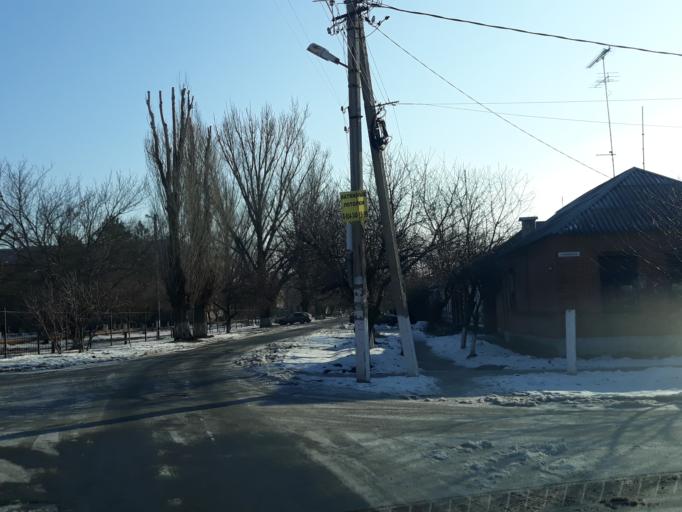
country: RU
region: Rostov
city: Taganrog
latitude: 47.2409
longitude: 38.8746
